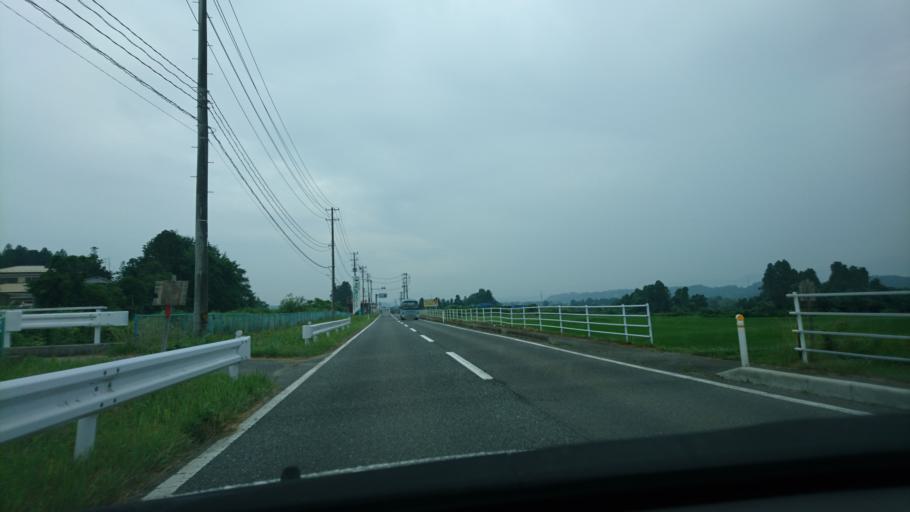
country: JP
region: Miyagi
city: Furukawa
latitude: 38.7309
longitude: 140.9951
